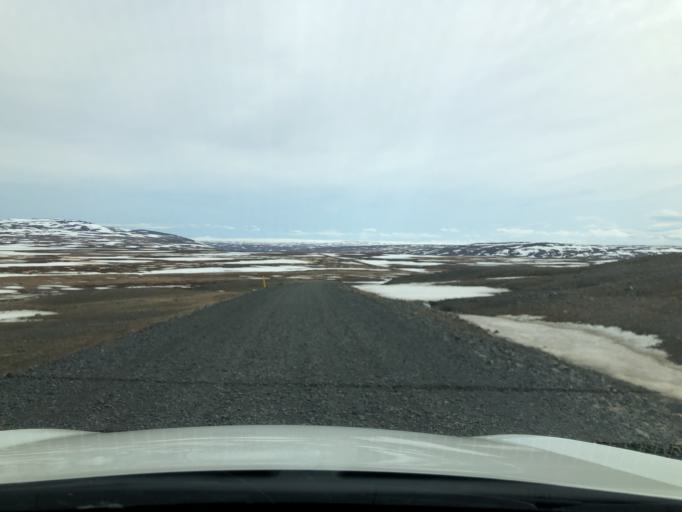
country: IS
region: East
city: Egilsstadir
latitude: 65.3084
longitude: -15.3619
